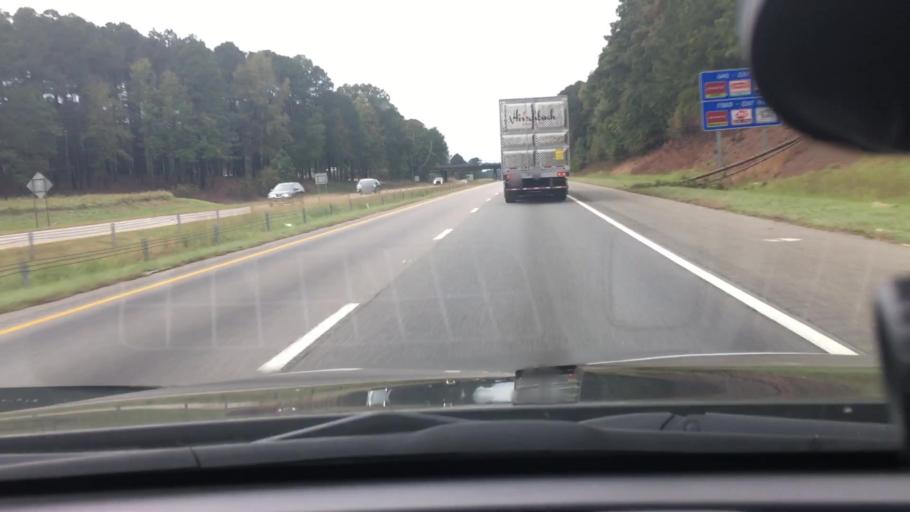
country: US
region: North Carolina
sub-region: Wake County
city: Apex
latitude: 35.7247
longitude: -78.8199
